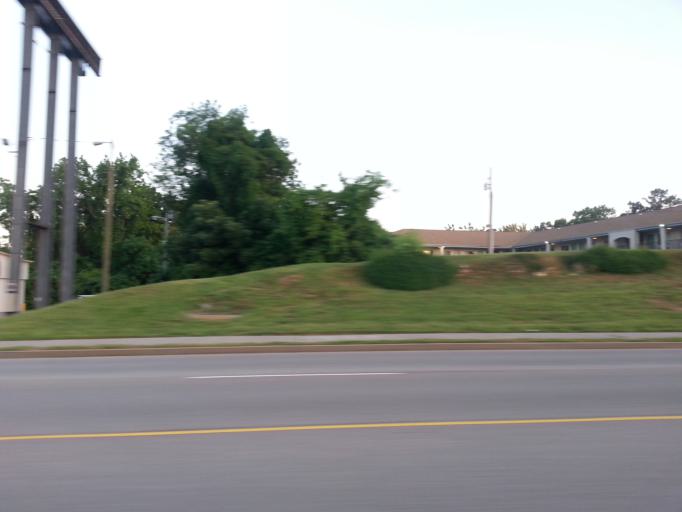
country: US
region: Tennessee
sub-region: Knox County
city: Knoxville
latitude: 35.9391
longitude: -84.0062
